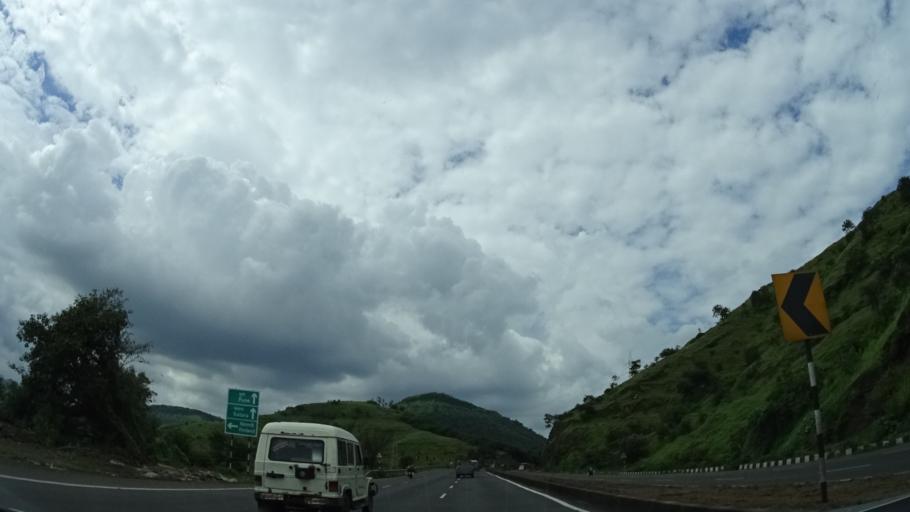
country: IN
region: Maharashtra
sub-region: Satara Division
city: Satara
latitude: 17.6521
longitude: 74.0138
